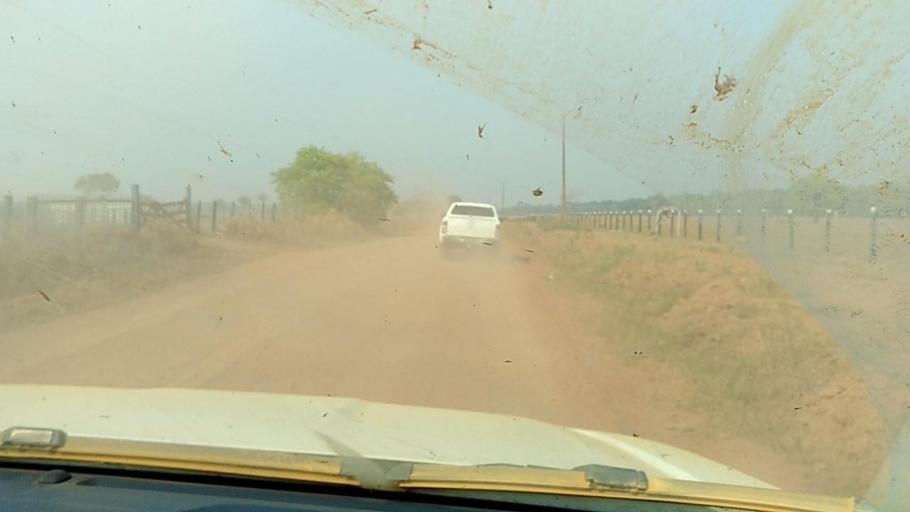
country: BR
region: Rondonia
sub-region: Porto Velho
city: Porto Velho
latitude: -8.7734
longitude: -64.0806
